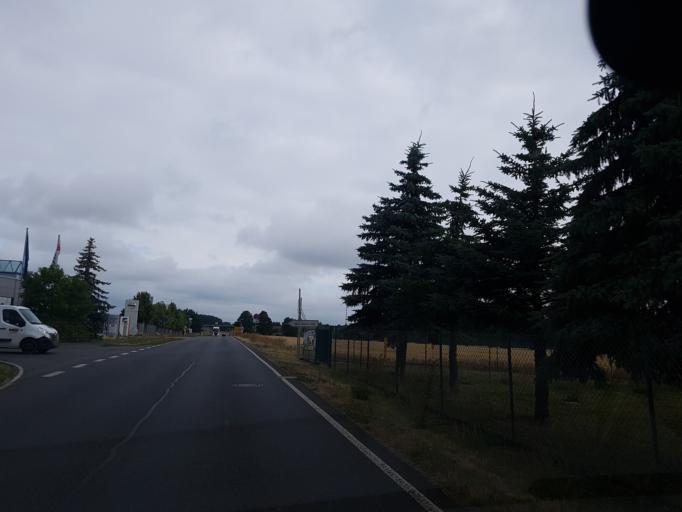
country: DE
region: Brandenburg
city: Luckau
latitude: 51.8600
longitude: 13.7366
